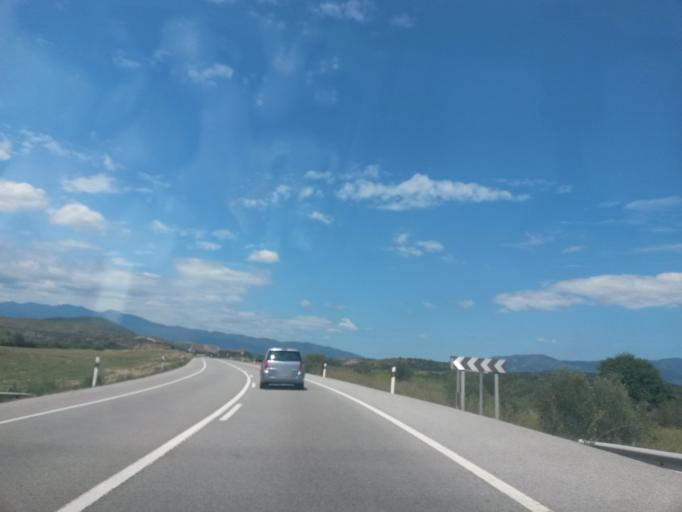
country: ES
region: Catalonia
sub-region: Provincia de Girona
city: Pont de Molins
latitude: 42.3272
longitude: 2.9328
